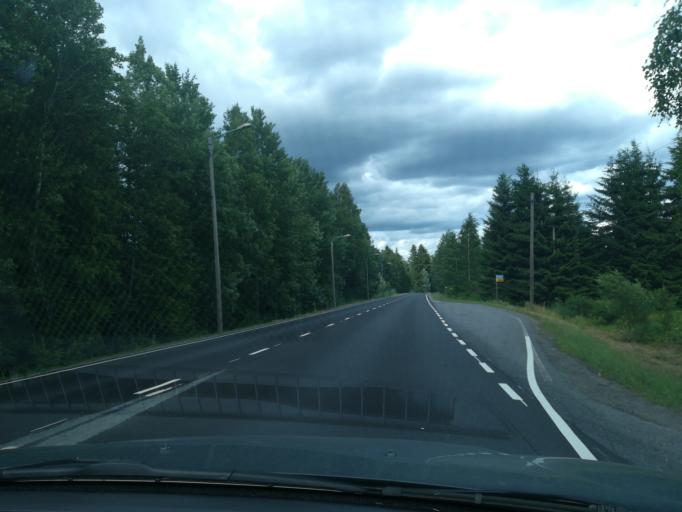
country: FI
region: Southern Savonia
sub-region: Mikkeli
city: Mikkeli
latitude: 61.6468
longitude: 27.0826
